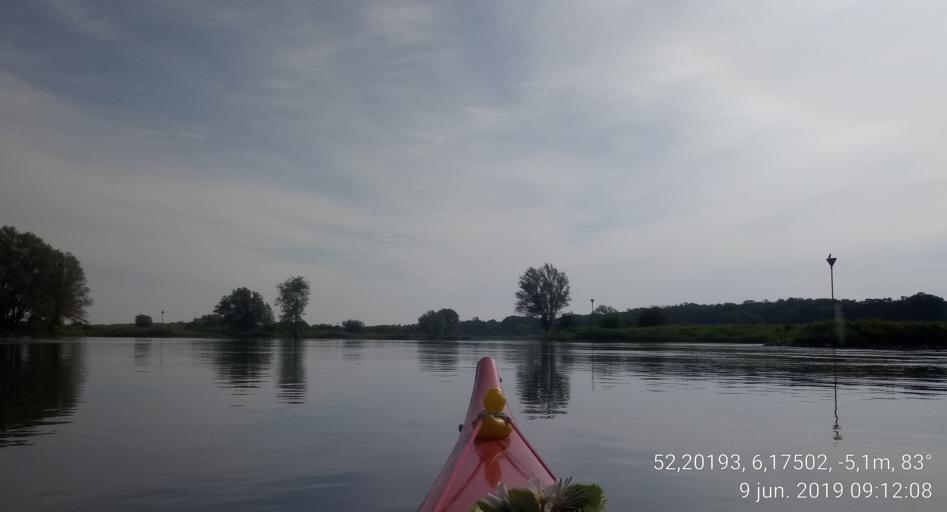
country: NL
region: Gelderland
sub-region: Gemeente Lochem
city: Gorssel
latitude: 52.2019
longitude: 6.1749
